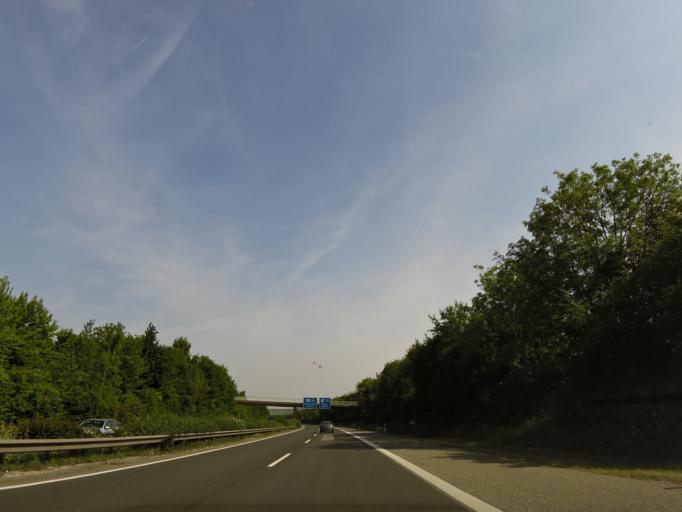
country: DE
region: Rheinland-Pfalz
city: Alzey
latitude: 49.7380
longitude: 8.1388
